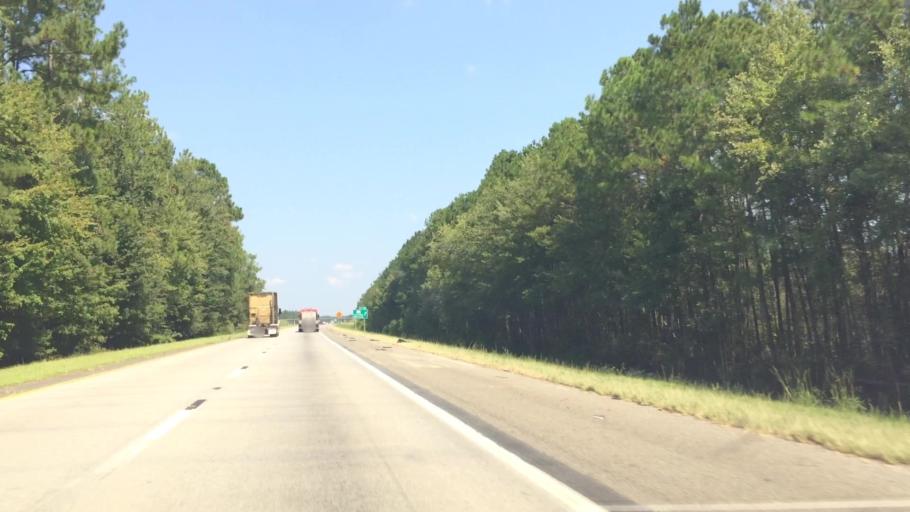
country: US
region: South Carolina
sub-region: Dorchester County
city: Saint George
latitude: 33.0762
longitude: -80.6565
